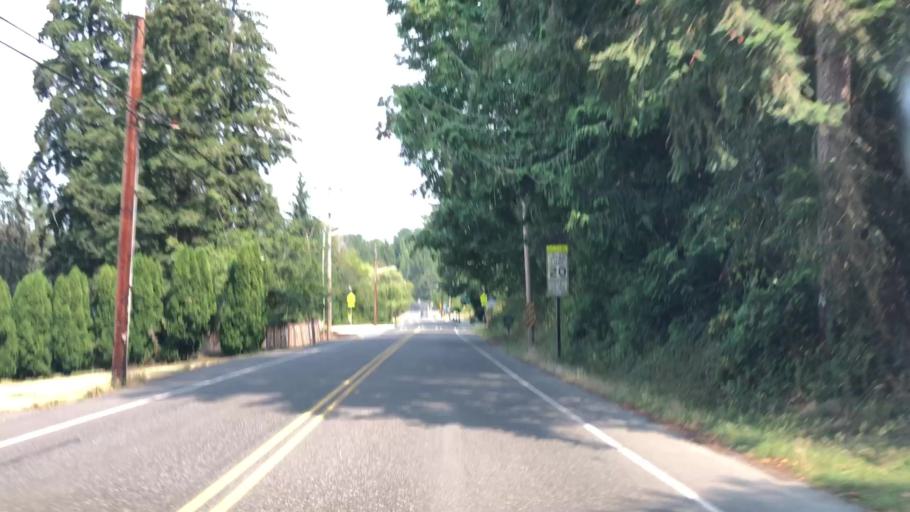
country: US
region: Washington
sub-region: King County
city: Kenmore
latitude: 47.7746
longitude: -122.2547
